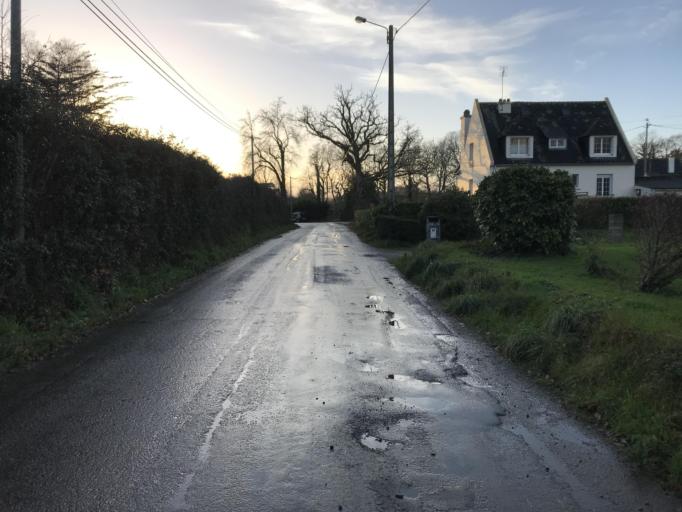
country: FR
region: Brittany
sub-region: Departement du Finistere
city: Hopital-Camfrout
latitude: 48.3302
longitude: -4.2398
